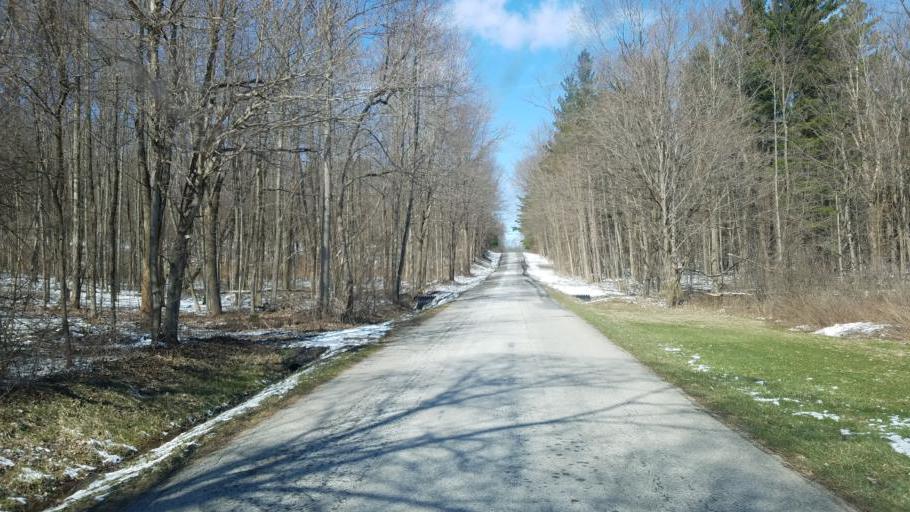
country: US
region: Ohio
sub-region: Richland County
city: Ontario
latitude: 40.7267
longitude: -82.6578
